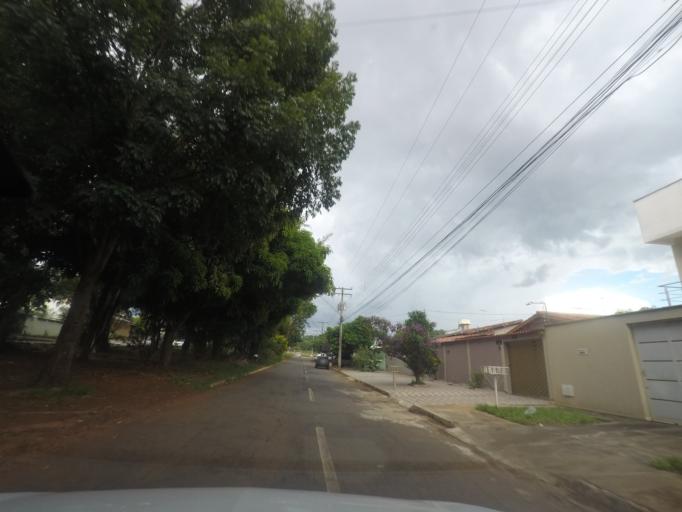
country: BR
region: Goias
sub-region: Goiania
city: Goiania
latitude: -16.6396
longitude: -49.2250
